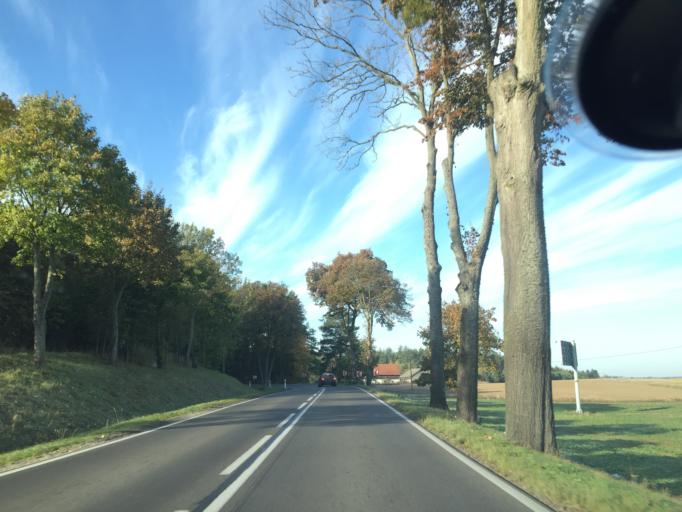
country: PL
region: Warmian-Masurian Voivodeship
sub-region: Powiat lidzbarski
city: Lidzbark Warminski
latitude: 54.1580
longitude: 20.6260
